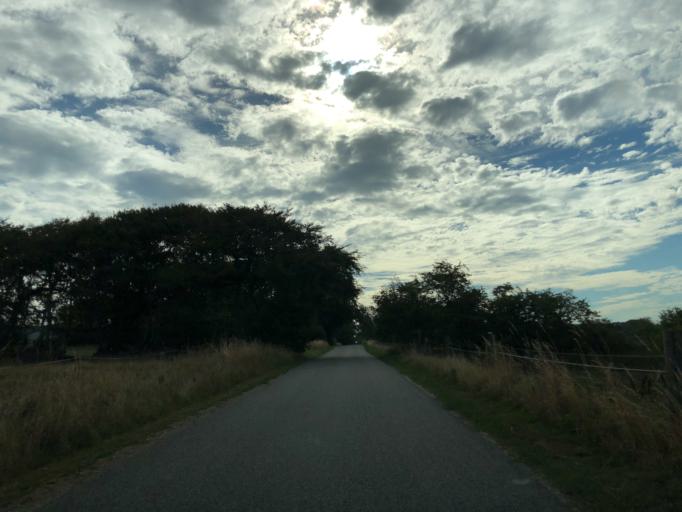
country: DK
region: Central Jutland
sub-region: Ringkobing-Skjern Kommune
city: Skjern
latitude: 56.0441
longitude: 8.4224
